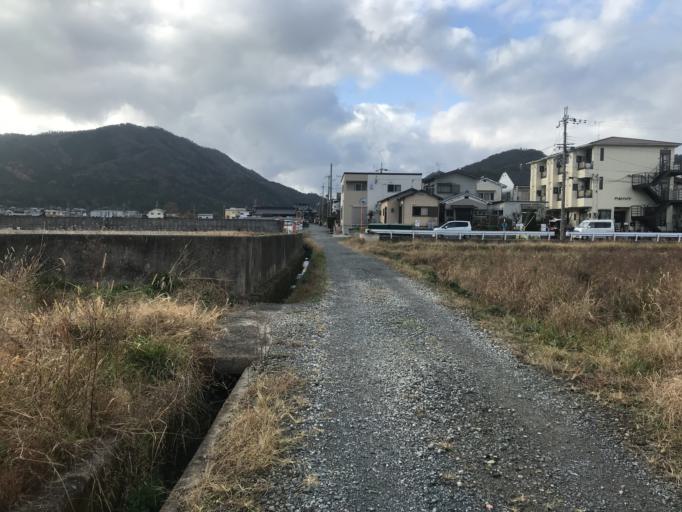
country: JP
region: Kyoto
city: Kameoka
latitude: 34.9954
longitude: 135.5464
